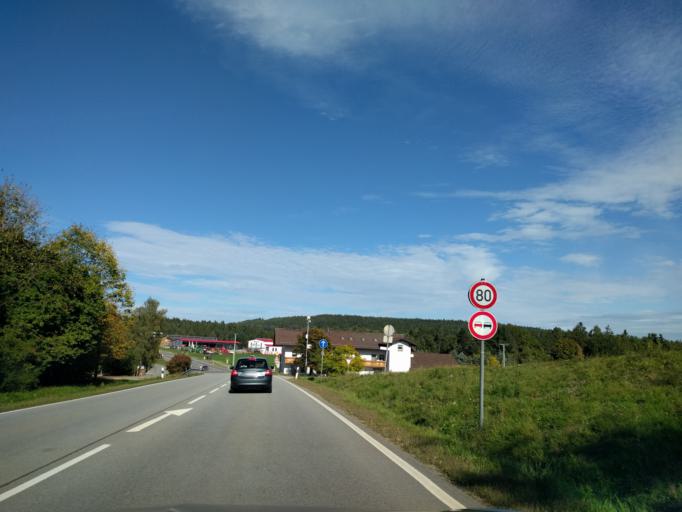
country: DE
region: Bavaria
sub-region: Lower Bavaria
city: Patersdorf
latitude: 49.0237
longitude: 12.9738
